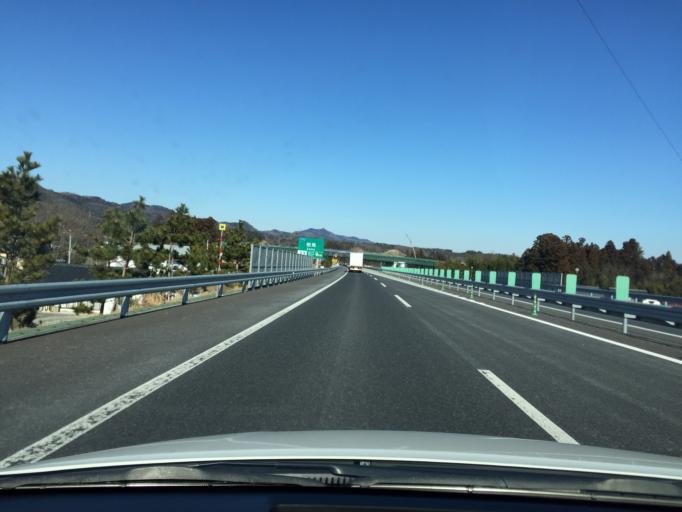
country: JP
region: Miyagi
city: Marumori
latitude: 37.7713
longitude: 140.9002
